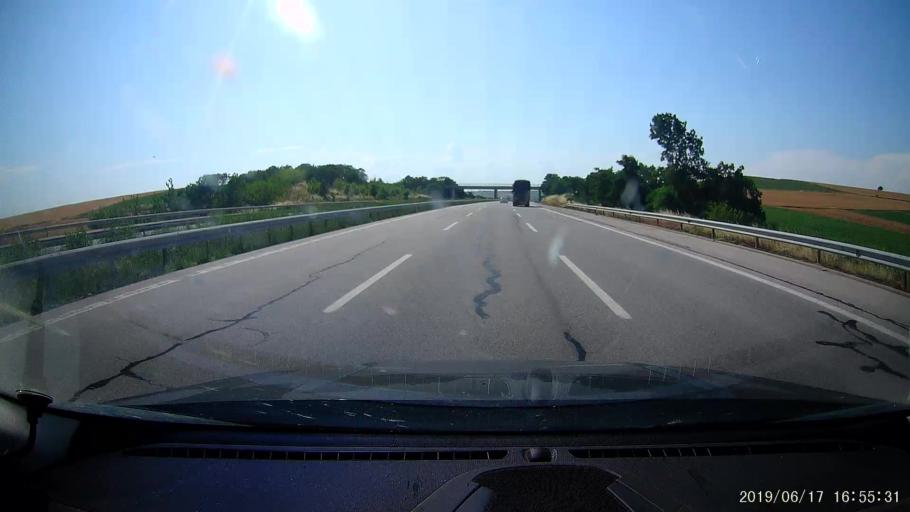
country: TR
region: Edirne
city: Haskoy
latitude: 41.5793
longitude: 26.9628
